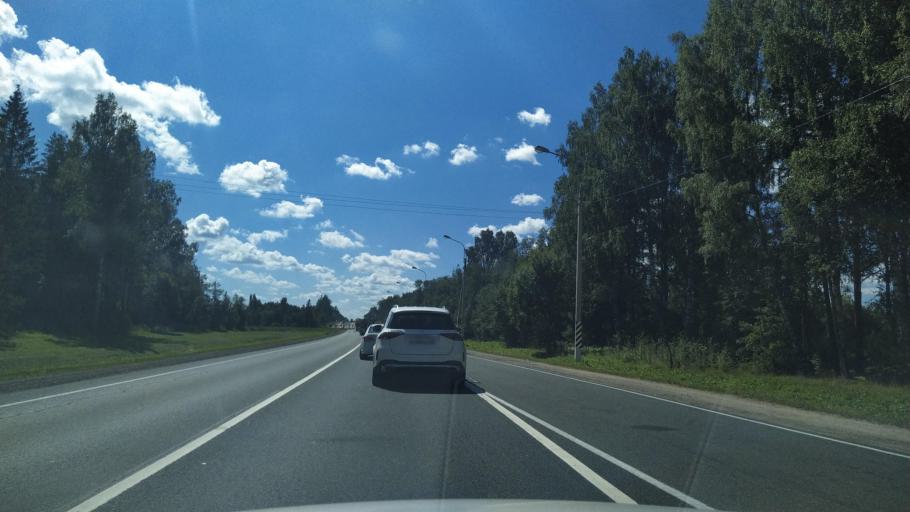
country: RU
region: Leningrad
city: Luga
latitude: 58.6231
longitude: 29.8327
